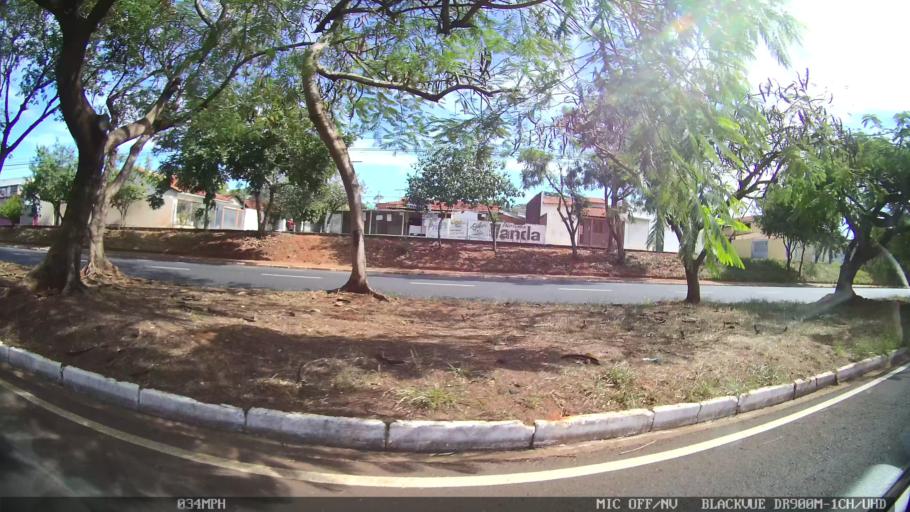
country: BR
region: Sao Paulo
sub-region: Sao Jose Do Rio Preto
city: Sao Jose do Rio Preto
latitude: -20.8294
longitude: -49.3511
